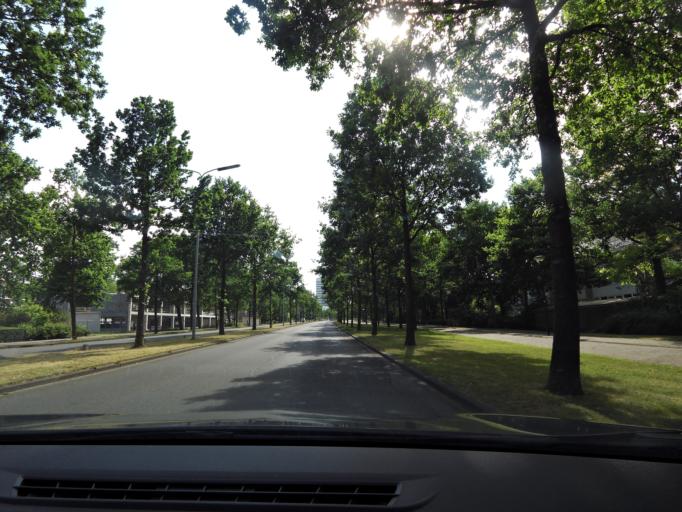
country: NL
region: South Holland
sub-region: Gemeente Rijswijk
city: Rijswijk
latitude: 52.0421
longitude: 4.3200
